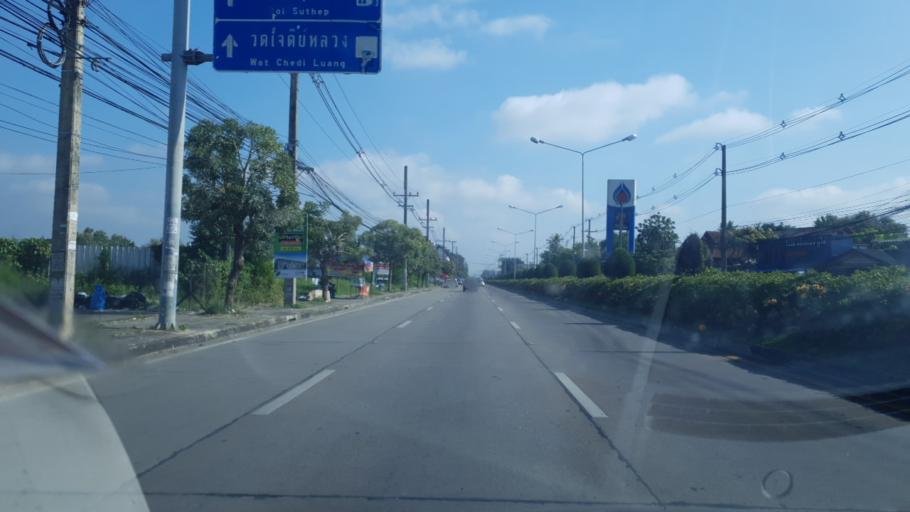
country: TH
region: Chiang Mai
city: Hang Dong
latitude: 18.7299
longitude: 98.9503
